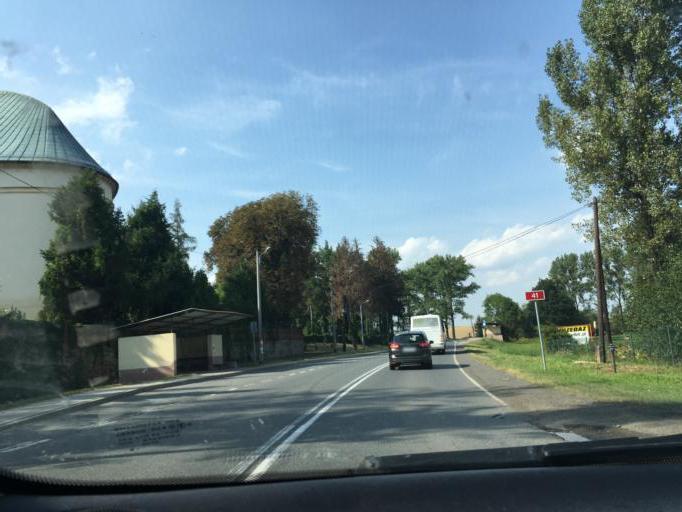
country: PL
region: Opole Voivodeship
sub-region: Powiat prudnicki
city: Laka Prudnicka
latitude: 50.3829
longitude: 17.5251
